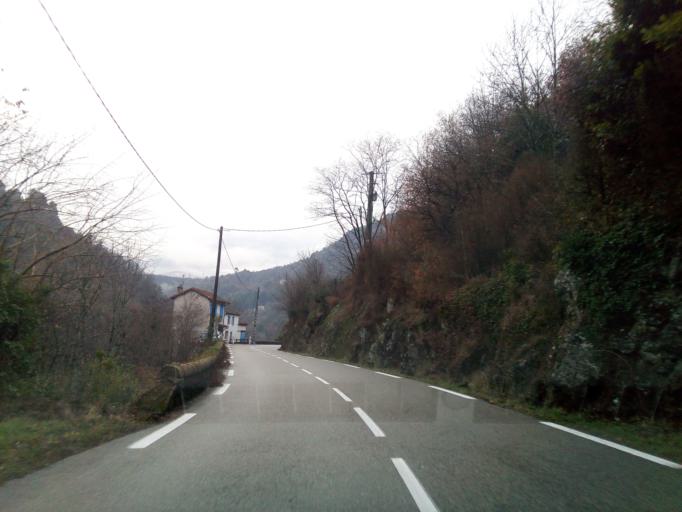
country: FR
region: Rhone-Alpes
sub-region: Departement de l'Ardeche
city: Saint-Sauveur-de-Montagut
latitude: 44.8355
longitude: 4.5770
